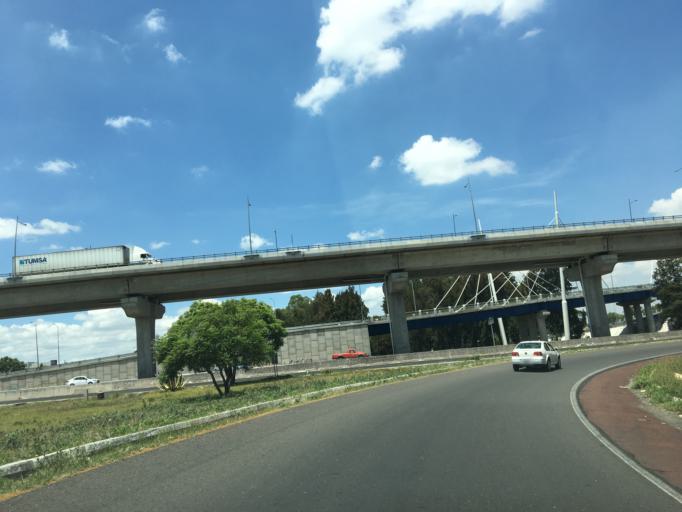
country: MX
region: Puebla
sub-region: Cuautlancingo
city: Sanctorum
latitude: 19.0974
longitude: -98.2284
